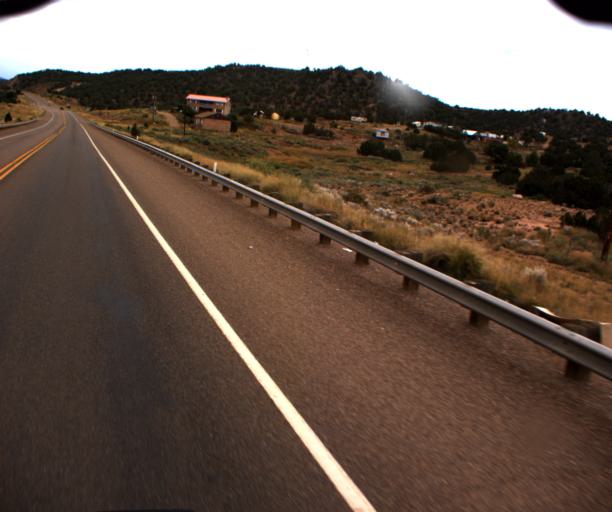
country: US
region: Arizona
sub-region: Navajo County
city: Taylor
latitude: 34.4098
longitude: -110.0797
